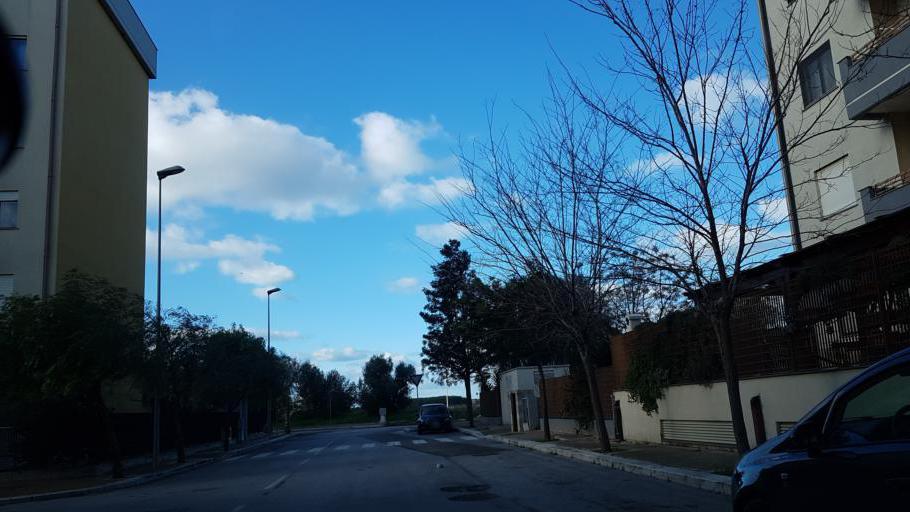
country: IT
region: Apulia
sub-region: Provincia di Brindisi
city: Brindisi
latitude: 40.6509
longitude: 17.9214
